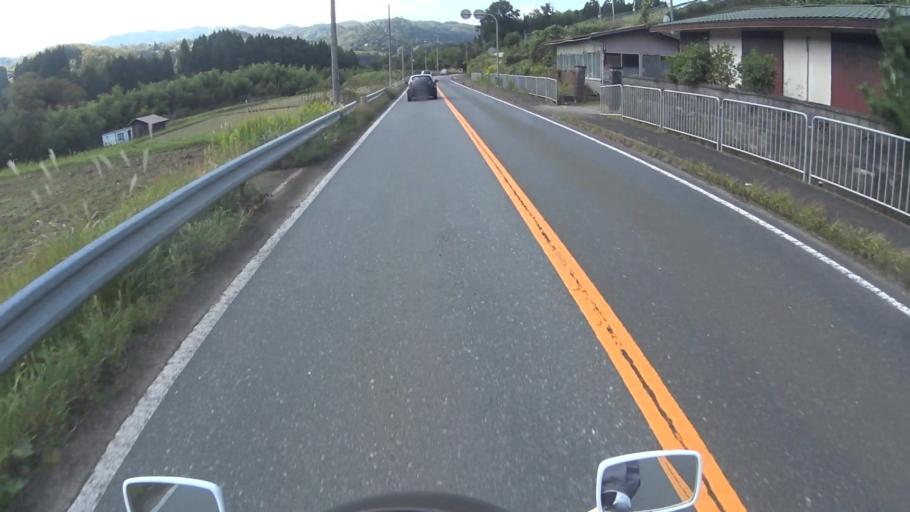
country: JP
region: Kyoto
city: Ayabe
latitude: 35.2907
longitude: 135.3000
